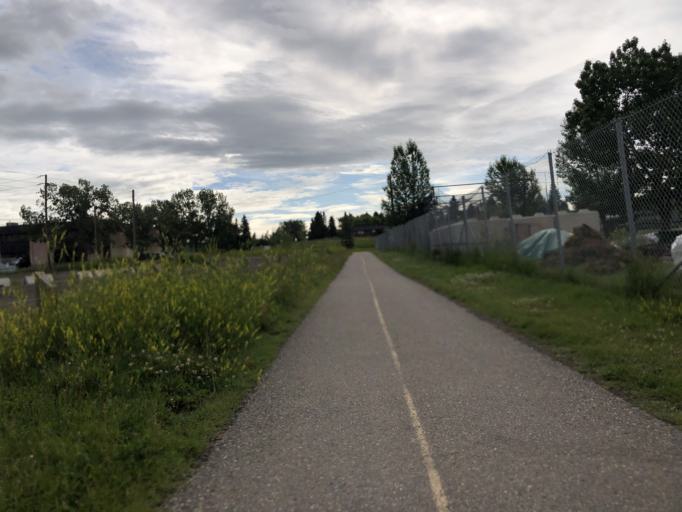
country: CA
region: Alberta
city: Calgary
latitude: 51.0740
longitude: -114.0248
